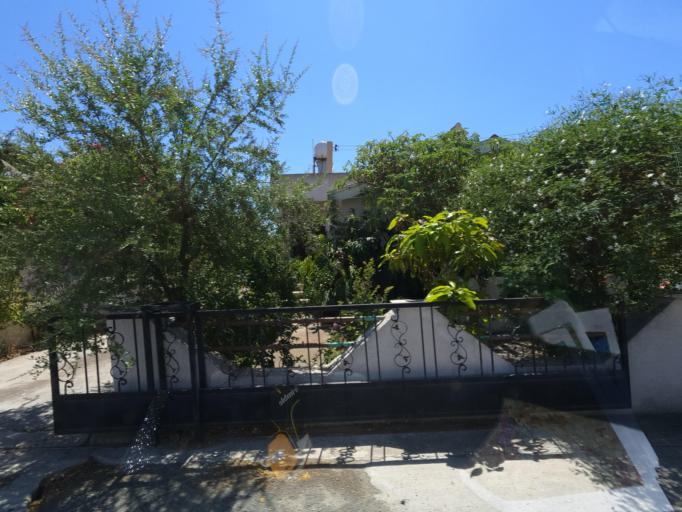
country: CY
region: Larnaka
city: Pyla
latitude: 35.0079
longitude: 33.6906
